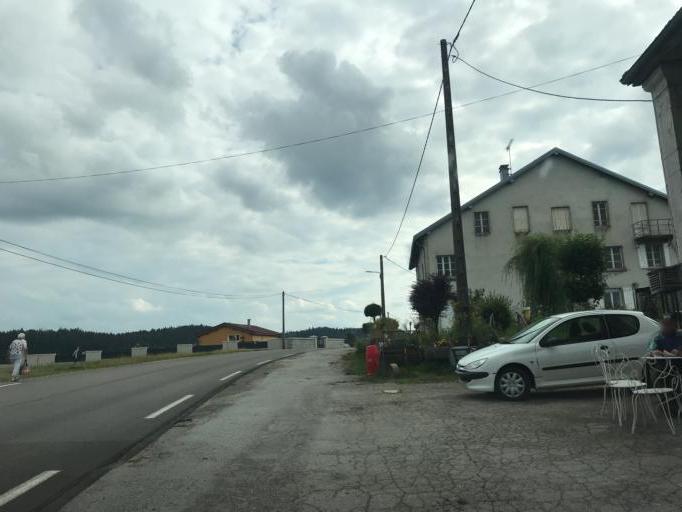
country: FR
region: Franche-Comte
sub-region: Departement du Jura
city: Valfin-les-Saint-Claude
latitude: 46.5072
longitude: 5.8674
